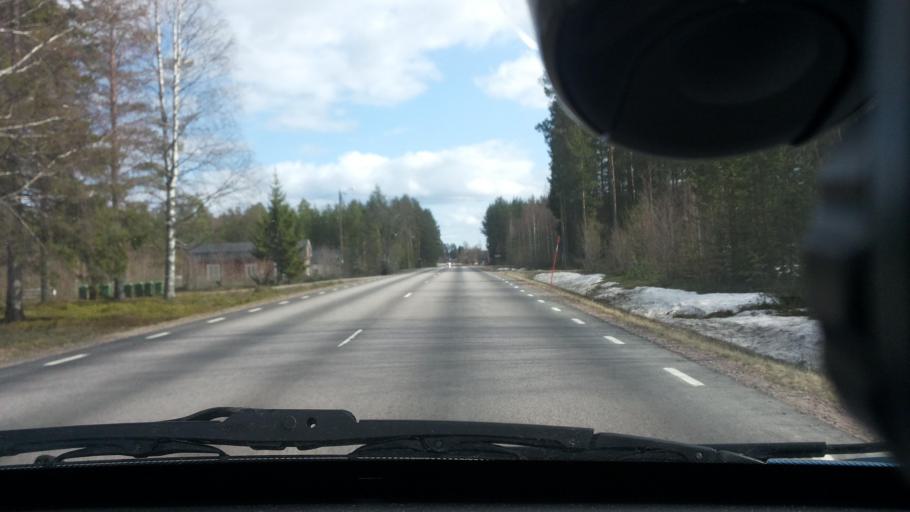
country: SE
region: Norrbotten
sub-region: Lulea Kommun
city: Sodra Sunderbyn
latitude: 65.6482
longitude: 21.8779
